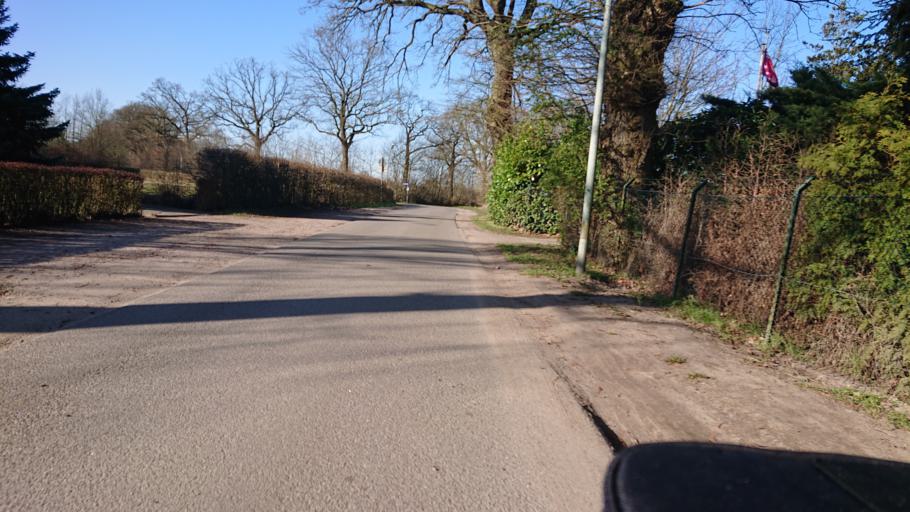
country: DE
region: Schleswig-Holstein
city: Hasloh
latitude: 53.6602
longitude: 9.8925
